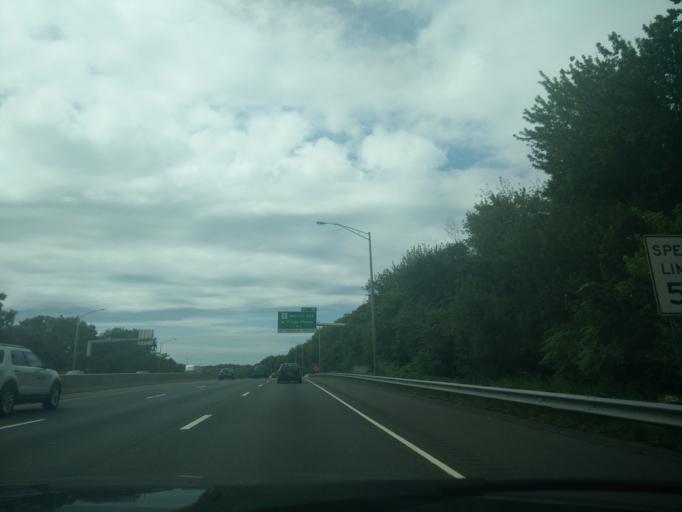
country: US
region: Connecticut
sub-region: New Haven County
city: Milford
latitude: 41.2364
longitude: -73.0489
